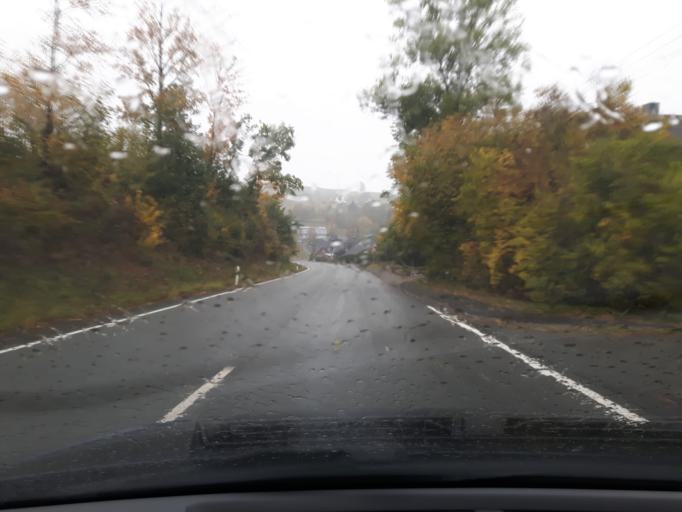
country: DE
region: North Rhine-Westphalia
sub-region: Regierungsbezirk Arnsberg
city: Bad Berleburg
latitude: 50.9893
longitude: 8.3933
